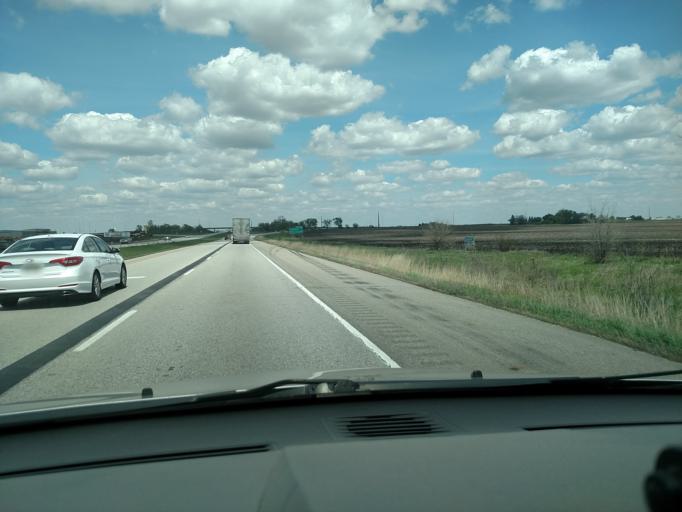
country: US
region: Iowa
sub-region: Polk County
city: Ankeny
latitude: 41.7842
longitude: -93.5705
